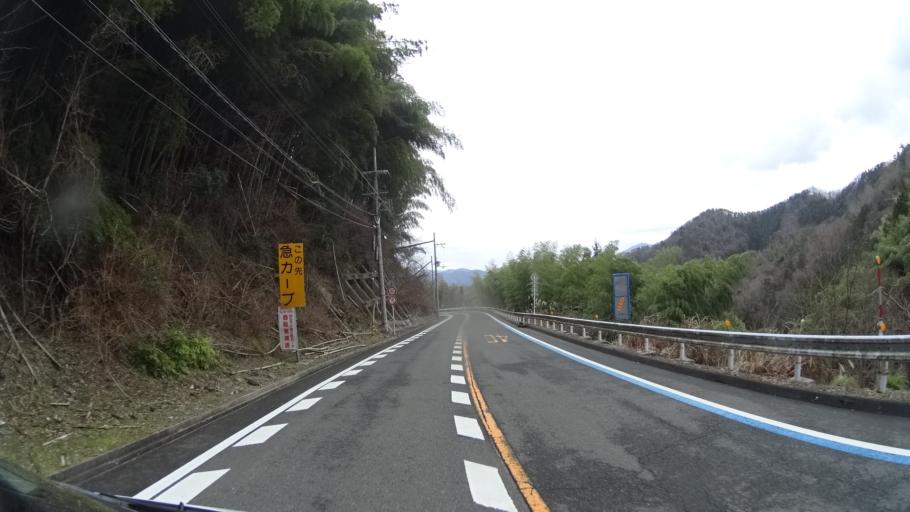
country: JP
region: Kyoto
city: Maizuru
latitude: 35.4346
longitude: 135.4003
